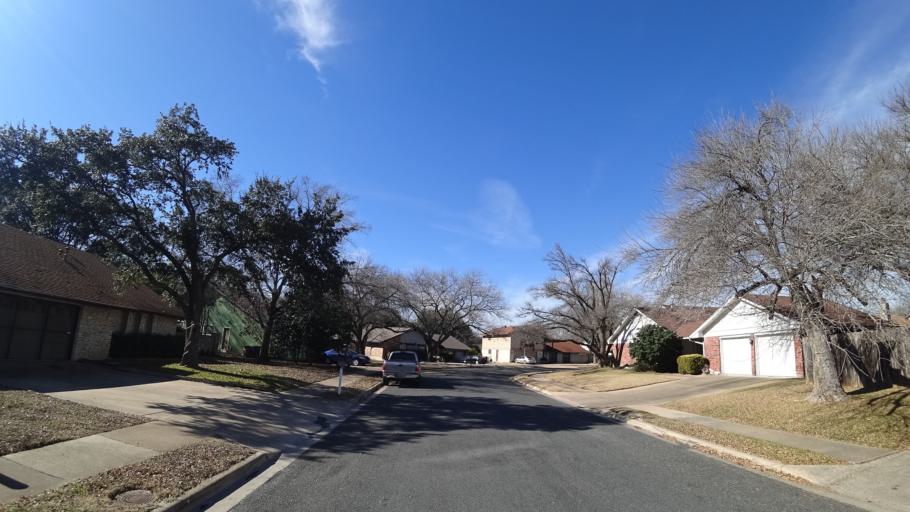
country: US
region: Texas
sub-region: Travis County
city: Wells Branch
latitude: 30.3782
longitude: -97.7003
